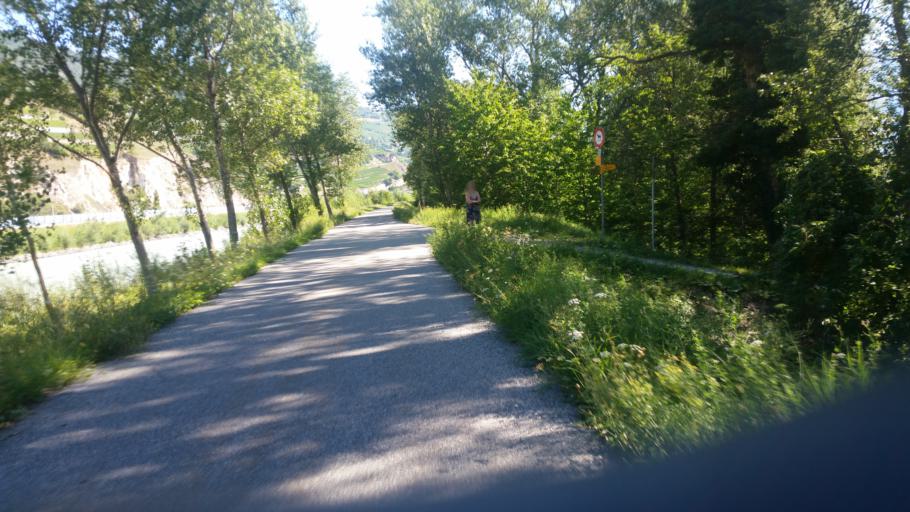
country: CH
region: Valais
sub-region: Sierre District
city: Grone
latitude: 46.2615
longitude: 7.4533
